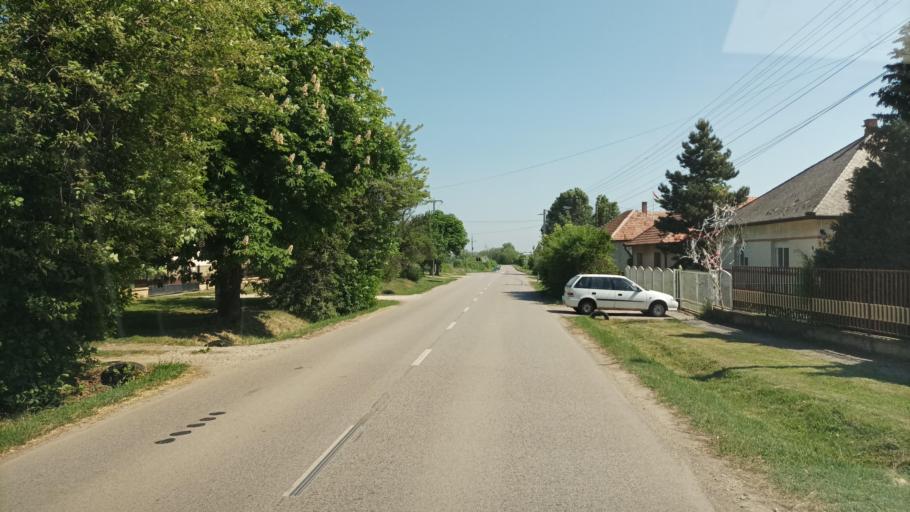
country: HU
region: Pest
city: Uri
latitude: 47.4224
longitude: 19.5213
